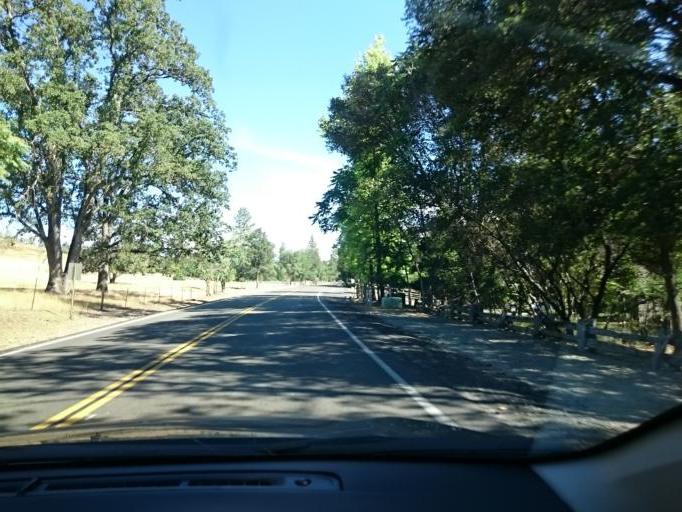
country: US
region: California
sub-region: Tuolumne County
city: Columbia
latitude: 38.0469
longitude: -120.4108
